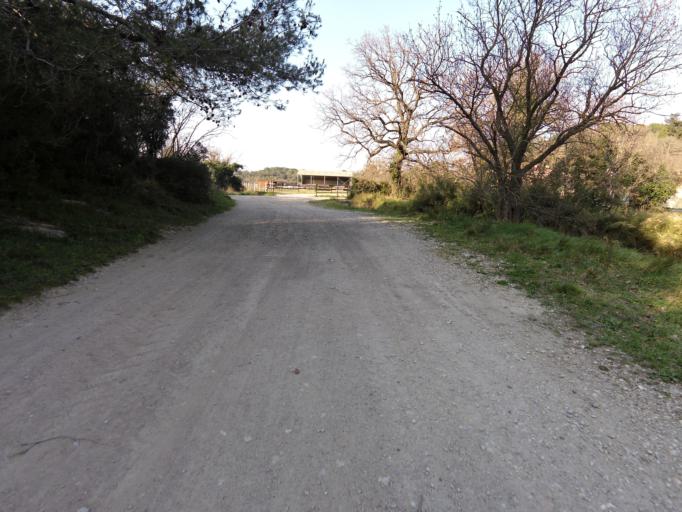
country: FR
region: Languedoc-Roussillon
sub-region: Departement du Gard
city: Aubais
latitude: 43.7392
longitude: 4.1586
